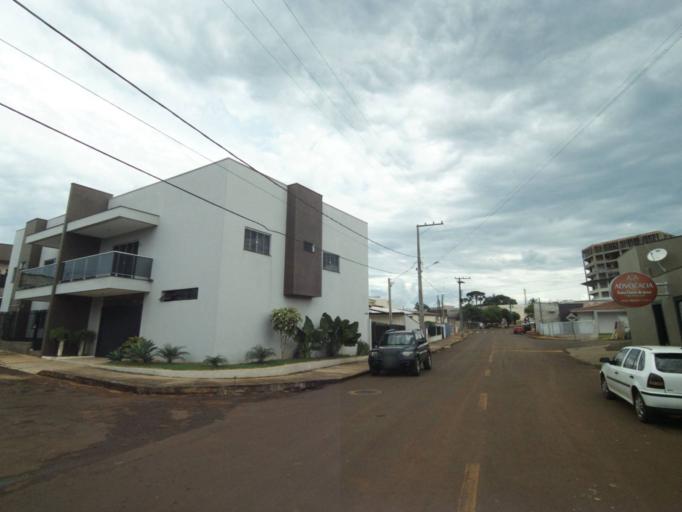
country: BR
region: Parana
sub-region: Guaraniacu
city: Guaraniacu
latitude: -25.0971
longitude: -52.8687
